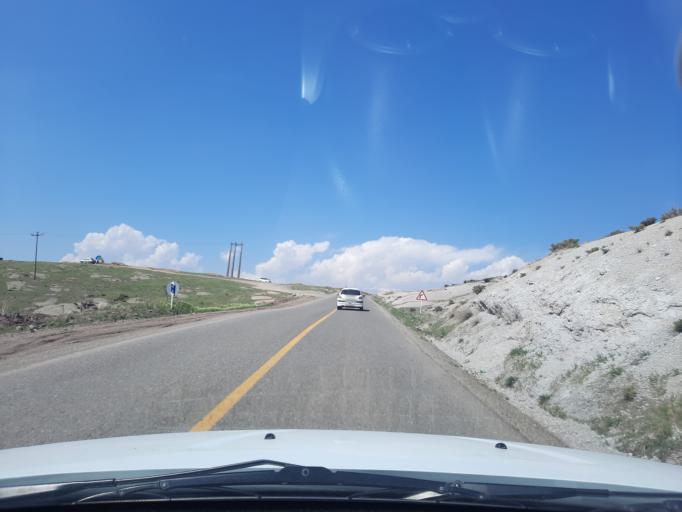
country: IR
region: Qazvin
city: Qazvin
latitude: 36.4098
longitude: 50.2348
